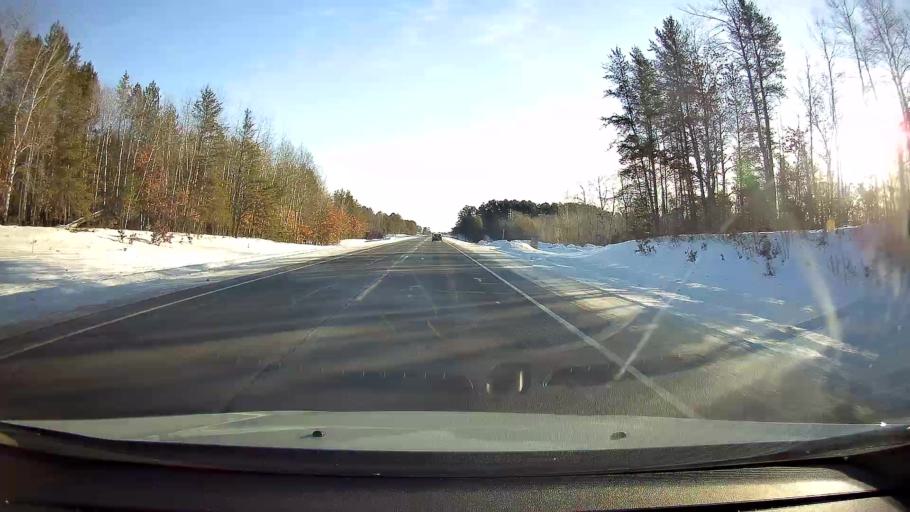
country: US
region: Wisconsin
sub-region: Washburn County
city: Spooner
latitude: 45.9104
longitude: -91.7782
